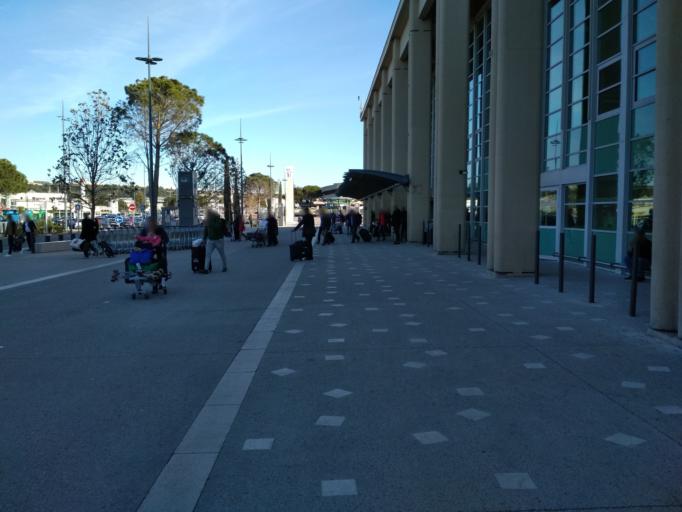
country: FR
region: Provence-Alpes-Cote d'Azur
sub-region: Departement des Bouches-du-Rhone
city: Saint-Victoret
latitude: 43.4418
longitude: 5.2221
